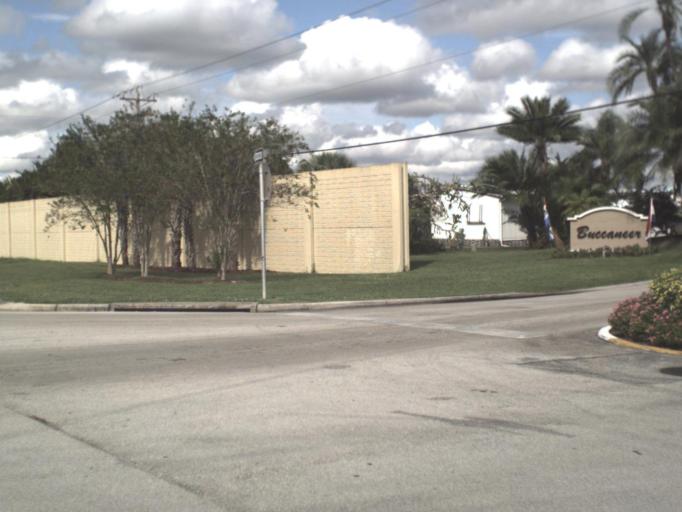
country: US
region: Florida
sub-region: Lee County
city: Palmona Park
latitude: 26.6913
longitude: -81.8873
